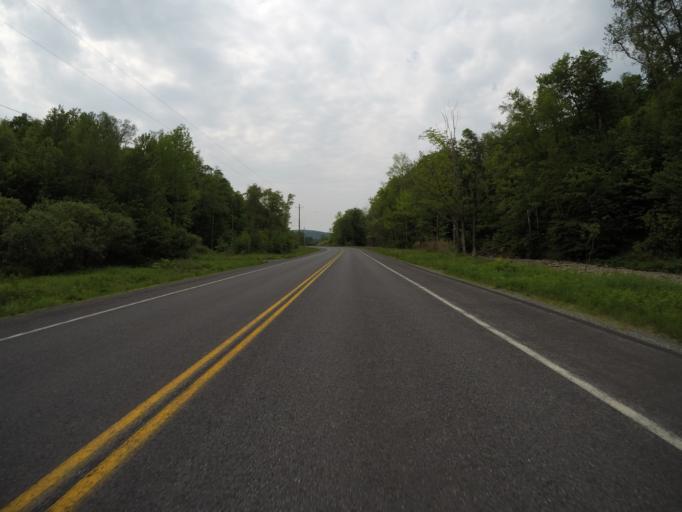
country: US
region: New York
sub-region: Sullivan County
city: Livingston Manor
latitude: 42.0078
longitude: -74.8920
